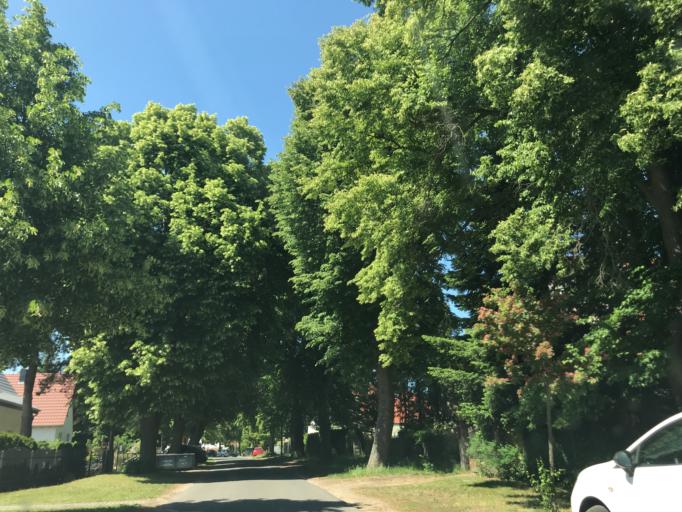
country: DE
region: Berlin
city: Falkenhagener Feld
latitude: 52.5695
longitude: 13.1411
